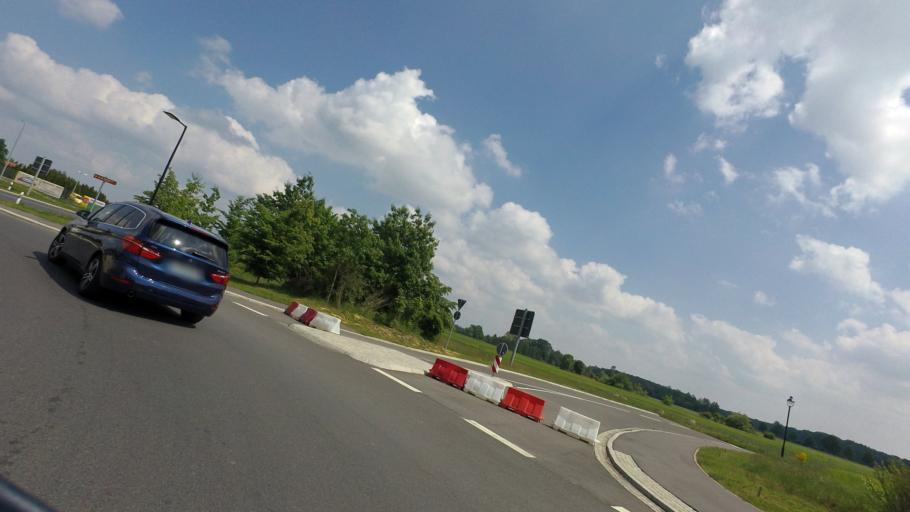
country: DE
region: Saxony
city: Schleife
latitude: 51.5465
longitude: 14.5464
